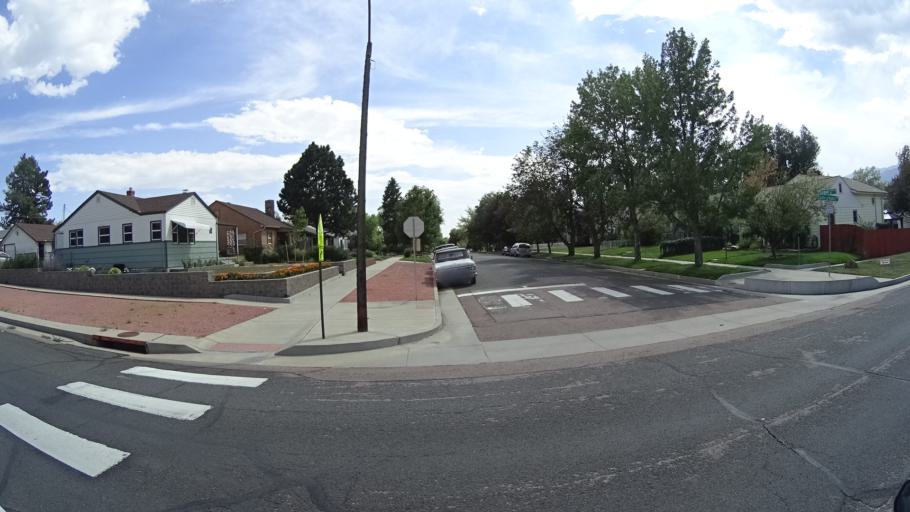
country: US
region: Colorado
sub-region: El Paso County
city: Colorado Springs
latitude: 38.8458
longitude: -104.7985
